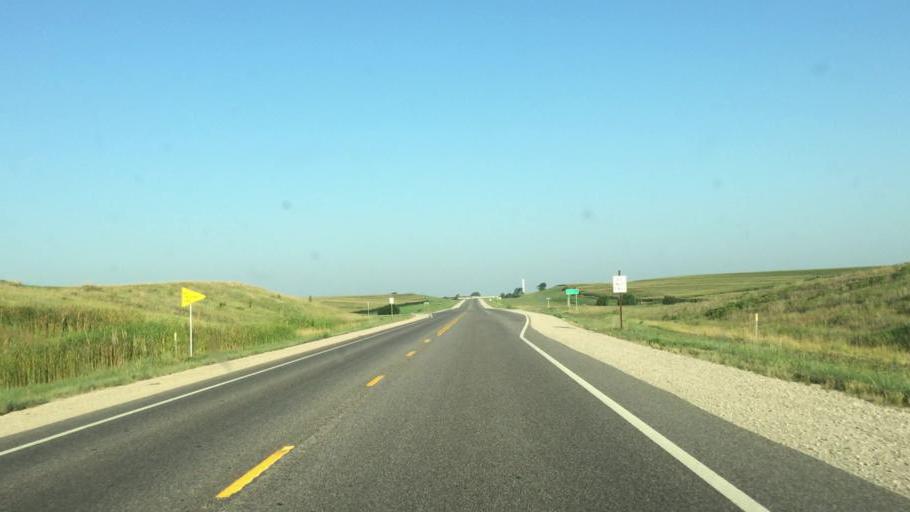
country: US
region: Kansas
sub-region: Doniphan County
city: Highland
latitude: 39.8421
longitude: -95.3195
